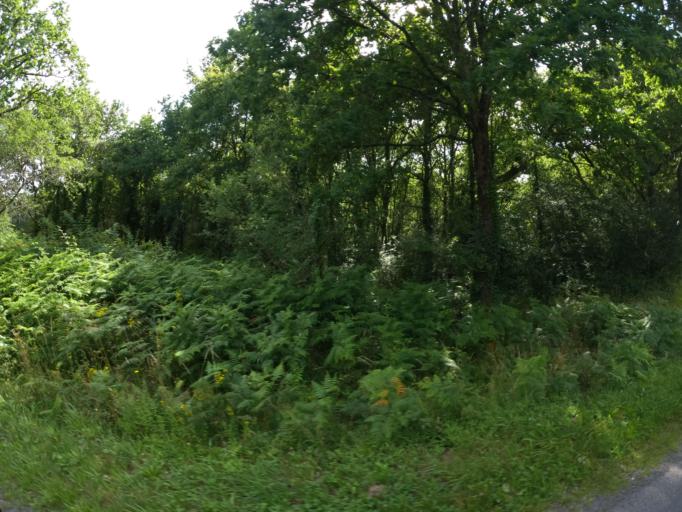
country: FR
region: Pays de la Loire
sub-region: Departement de la Loire-Atlantique
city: Geneston
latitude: 47.0565
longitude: -1.5235
